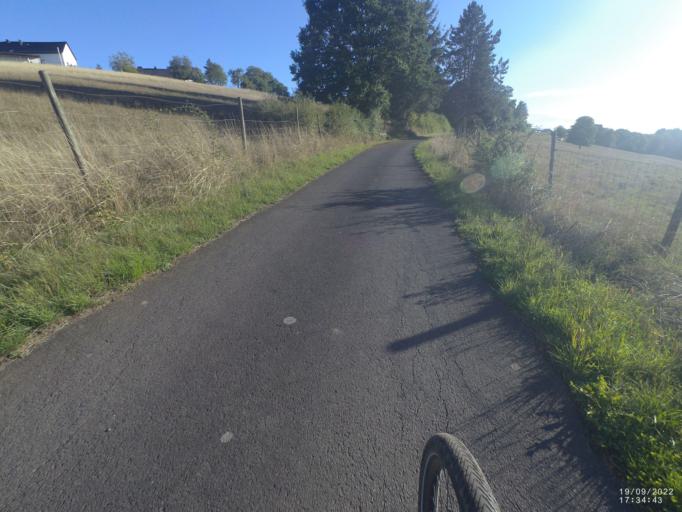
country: DE
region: Rheinland-Pfalz
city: Udersdorf
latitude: 50.1400
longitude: 6.8230
